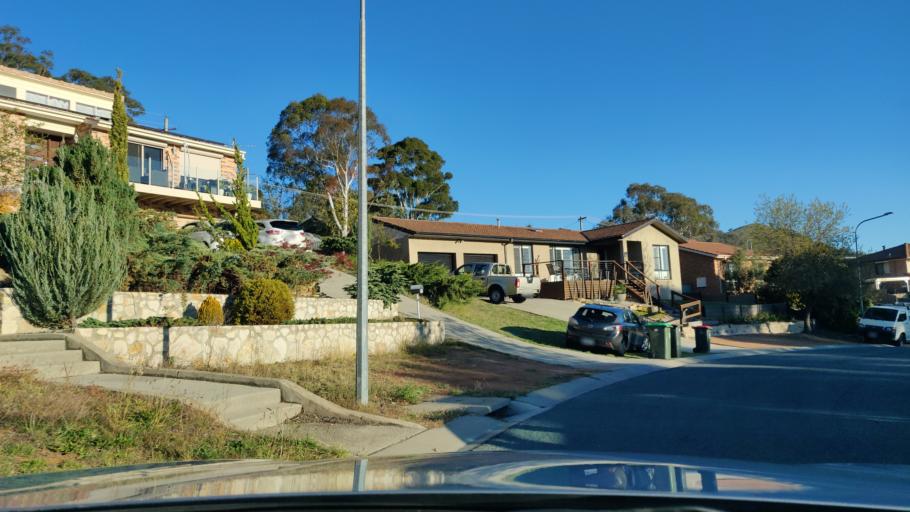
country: AU
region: Australian Capital Territory
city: Macarthur
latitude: -35.4444
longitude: 149.1278
